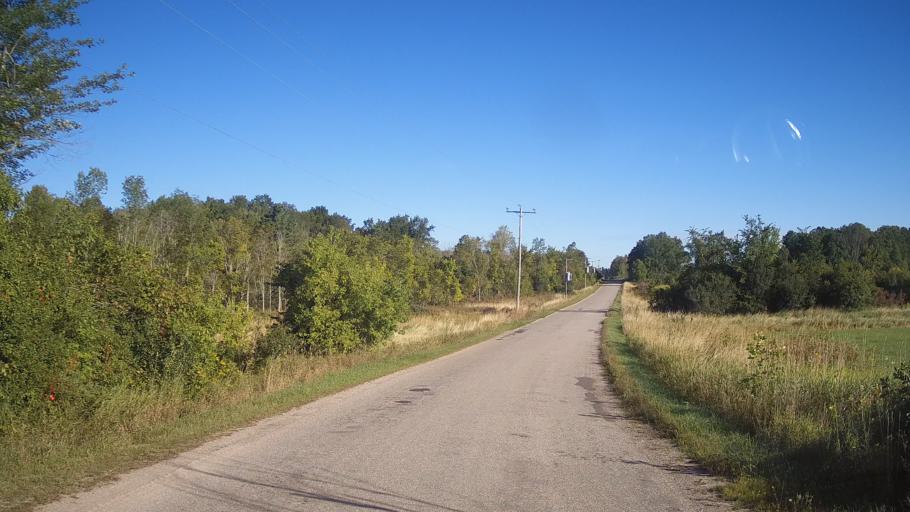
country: US
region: New York
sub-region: Jefferson County
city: Alexandria Bay
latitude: 44.4180
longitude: -75.9777
